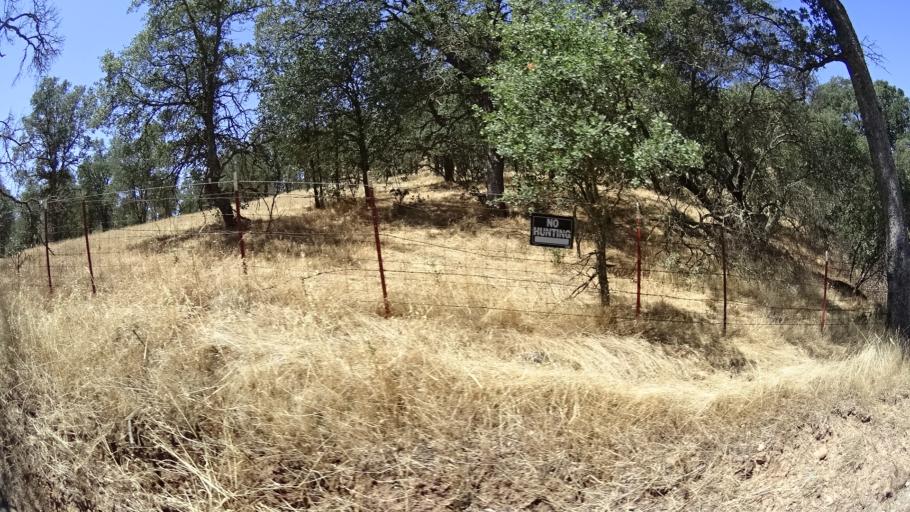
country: US
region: California
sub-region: Calaveras County
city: Rancho Calaveras
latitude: 38.1361
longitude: -120.8804
